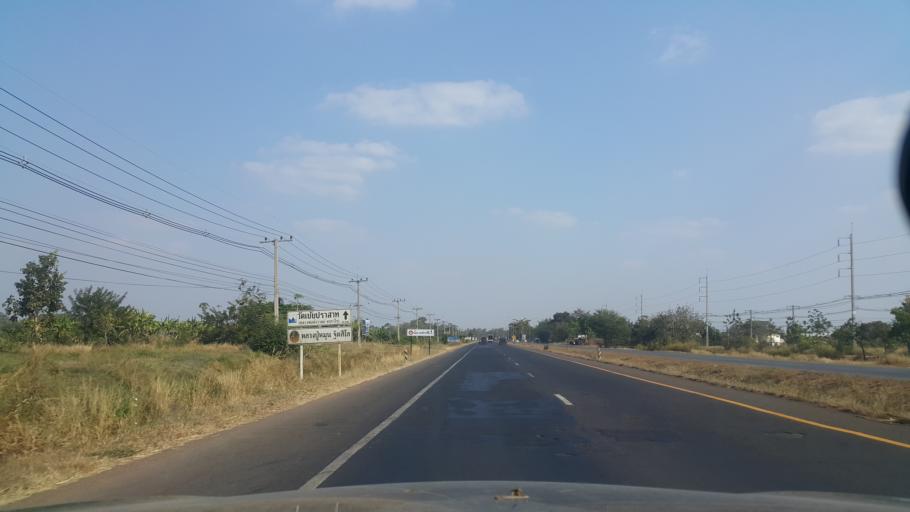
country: TH
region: Buriram
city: Nong Ki
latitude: 14.6945
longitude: 102.5072
